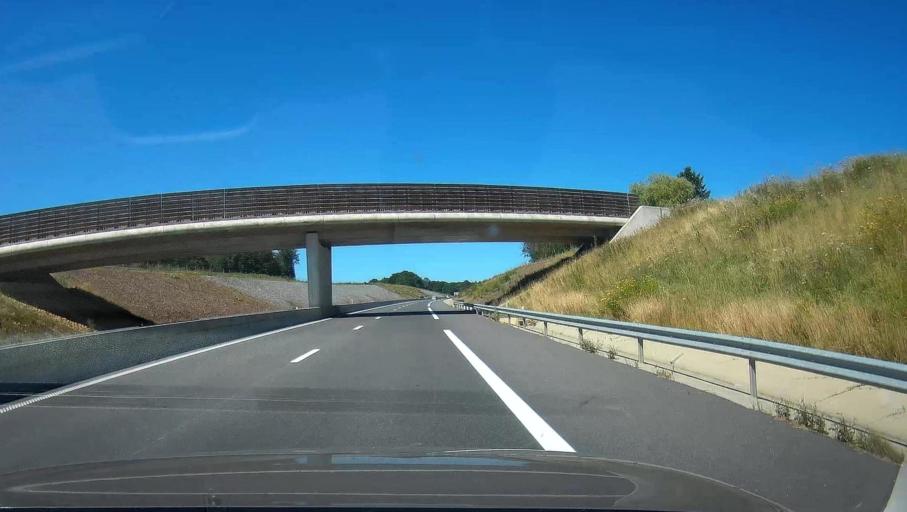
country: FR
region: Champagne-Ardenne
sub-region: Departement des Ardennes
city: Rimogne
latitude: 49.8225
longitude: 4.5131
